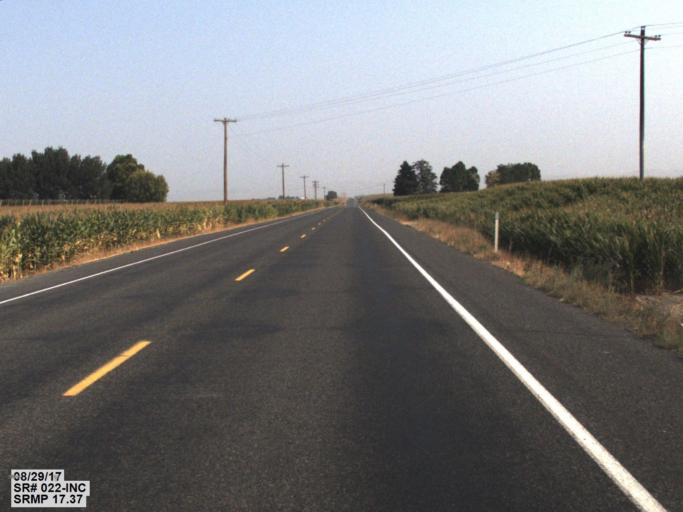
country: US
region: Washington
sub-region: Yakima County
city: Mabton
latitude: 46.2452
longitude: -120.1088
